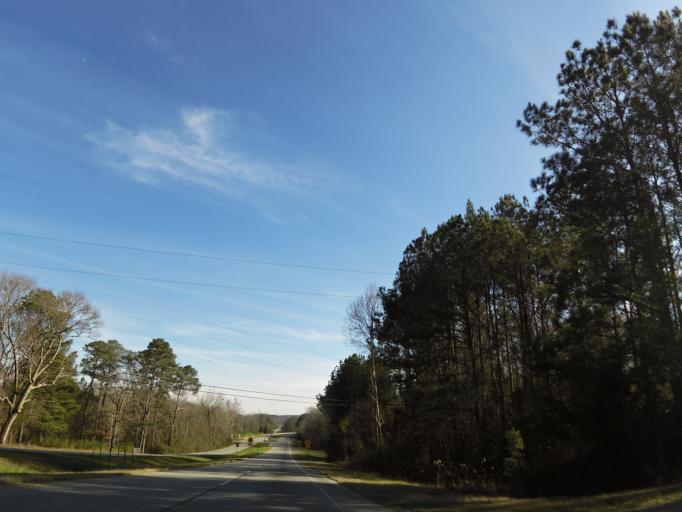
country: US
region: Georgia
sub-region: Chattahoochee County
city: Cusseta
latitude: 32.2858
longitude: -84.7633
